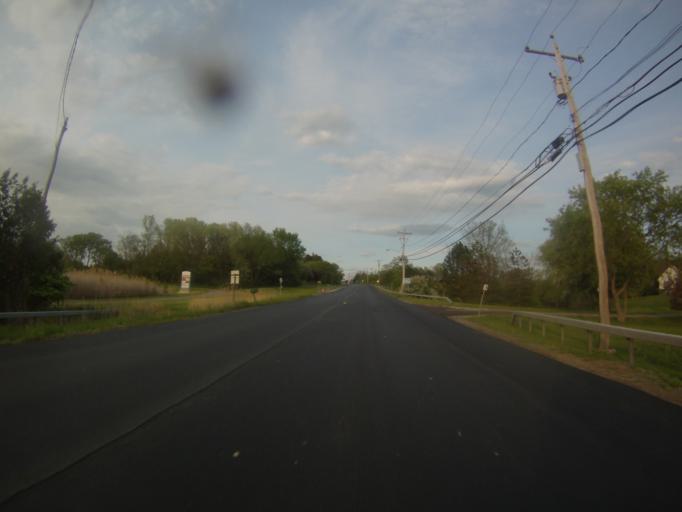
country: US
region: New York
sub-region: Essex County
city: Ticonderoga
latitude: 43.8463
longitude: -73.4410
